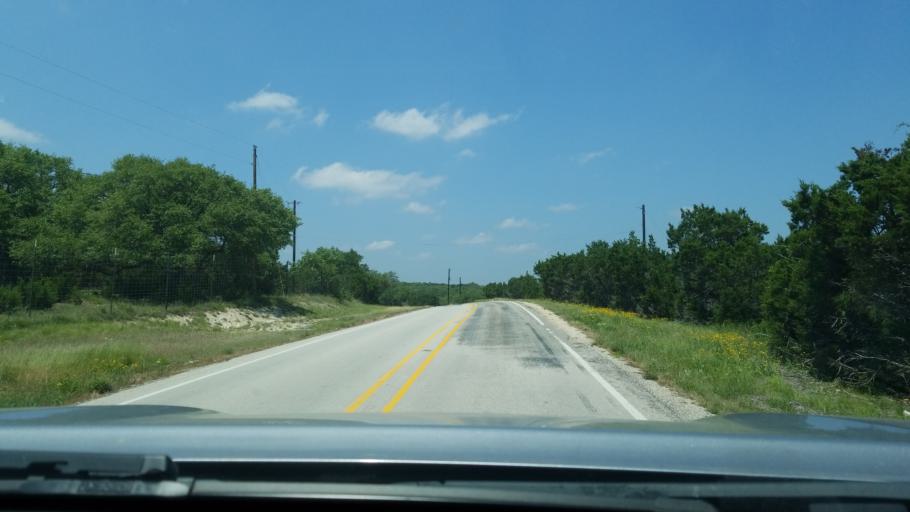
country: US
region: Texas
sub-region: Hays County
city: Woodcreek
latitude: 30.0897
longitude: -98.2288
